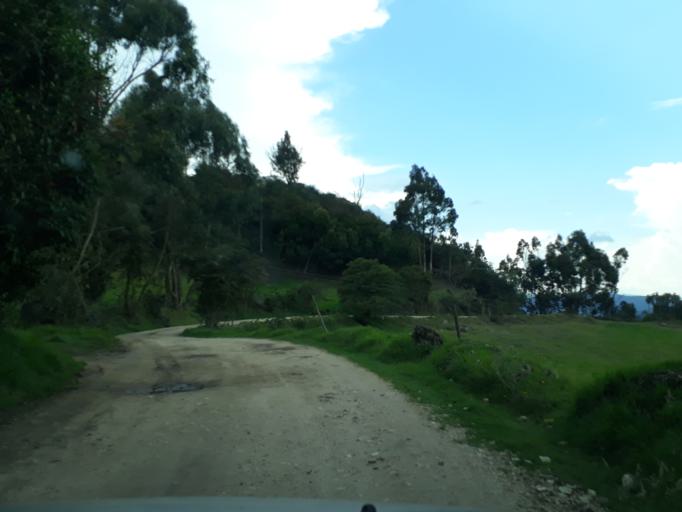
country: CO
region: Cundinamarca
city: Lenguazaque
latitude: 5.2543
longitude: -73.6837
